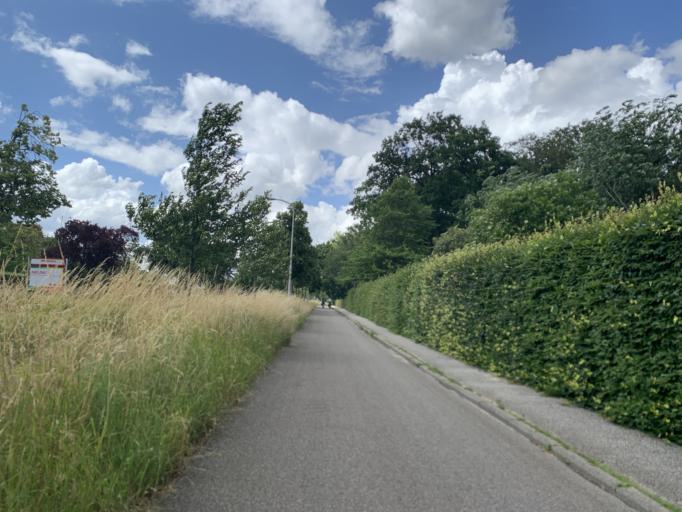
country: NL
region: Groningen
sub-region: Gemeente Haren
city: Haren
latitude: 53.1830
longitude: 6.5909
